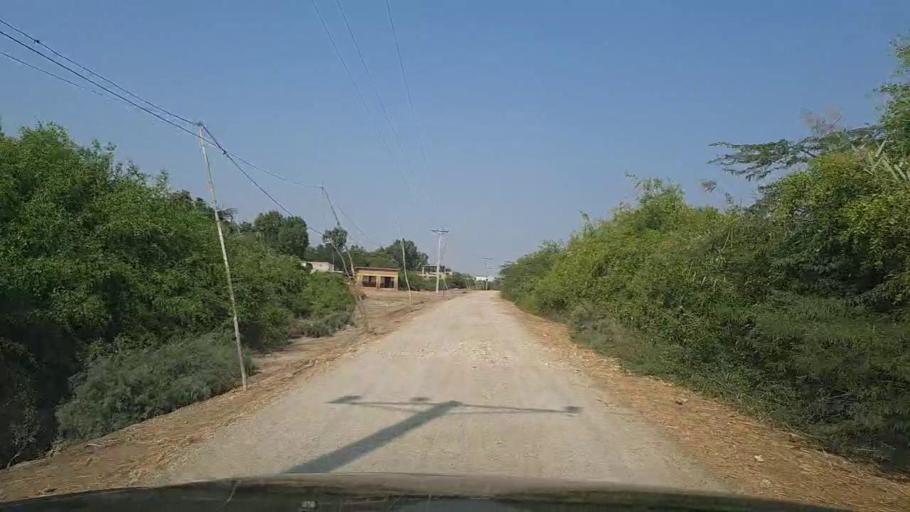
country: PK
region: Sindh
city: Thatta
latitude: 24.6140
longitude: 67.8203
